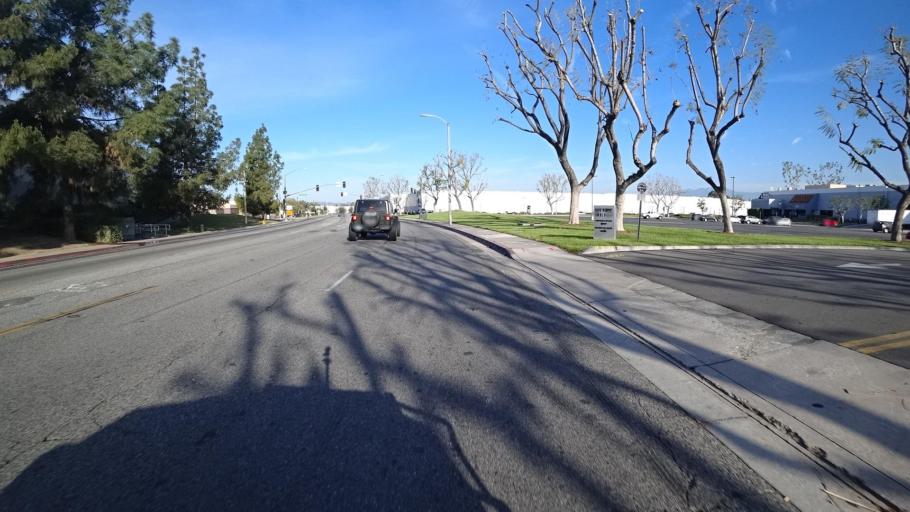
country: US
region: California
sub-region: Los Angeles County
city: South San Jose Hills
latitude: 34.0002
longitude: -117.9034
